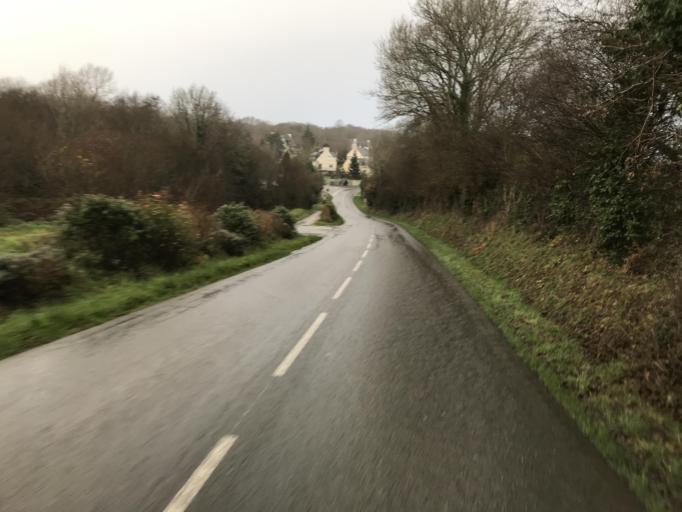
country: FR
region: Brittany
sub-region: Departement du Finistere
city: Loperhet
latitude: 48.3642
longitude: -4.3095
